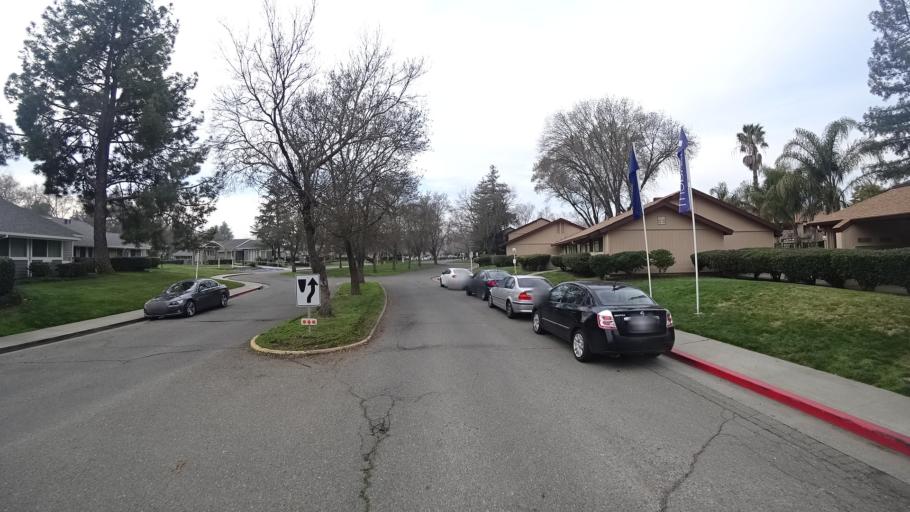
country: US
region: California
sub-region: Yolo County
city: Davis
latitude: 38.5598
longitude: -121.7401
